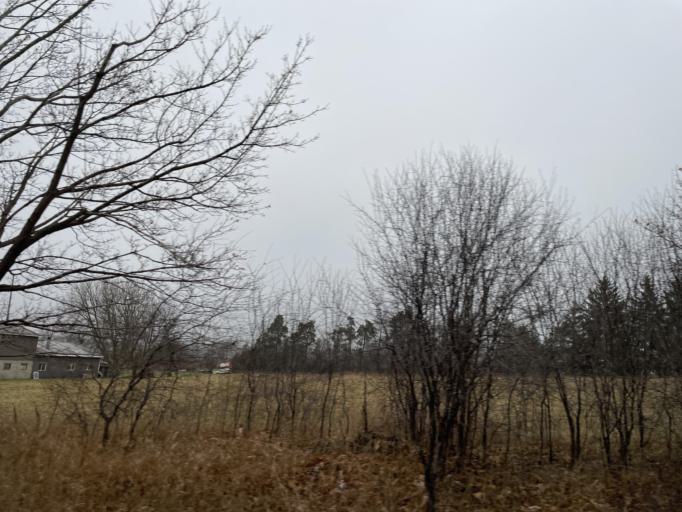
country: CA
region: Ontario
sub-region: Wellington County
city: Guelph
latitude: 43.5050
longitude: -80.3419
